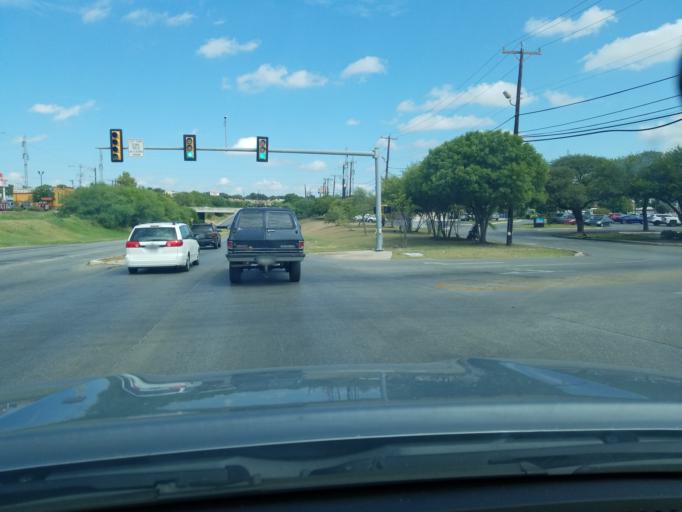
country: US
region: Texas
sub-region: Bexar County
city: Terrell Hills
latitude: 29.4922
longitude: -98.4324
